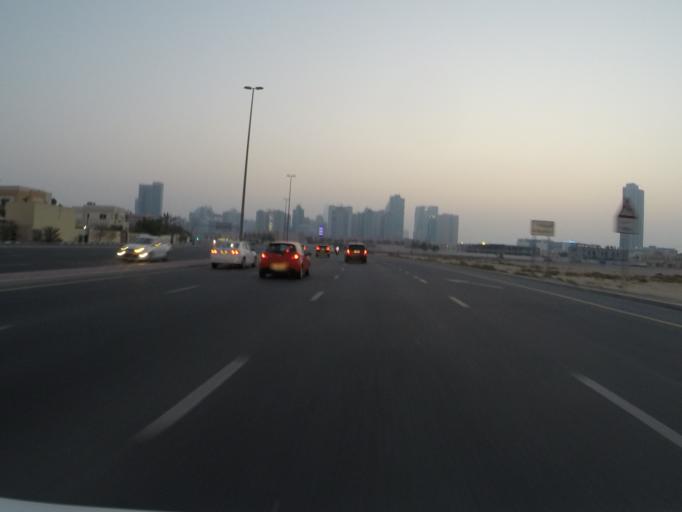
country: AE
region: Dubai
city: Dubai
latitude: 25.1053
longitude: 55.1901
